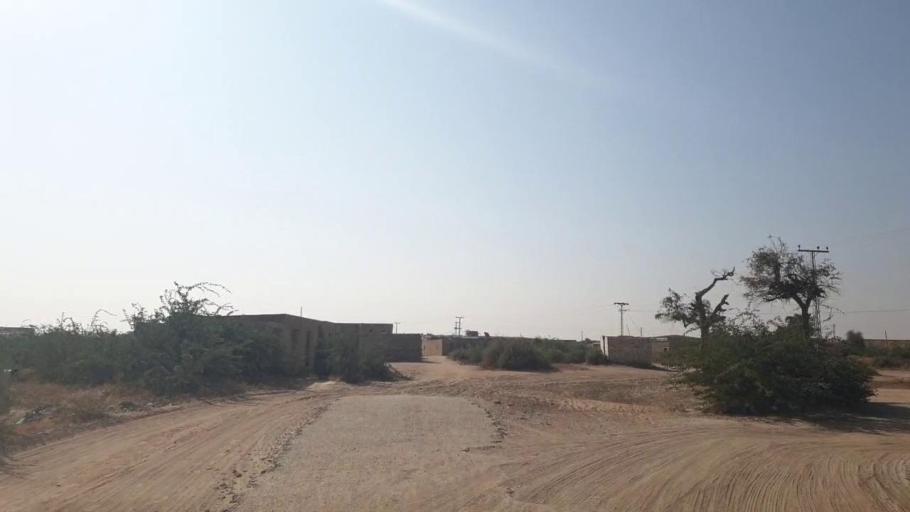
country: PK
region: Sindh
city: Thatta
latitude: 25.1349
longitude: 67.7722
